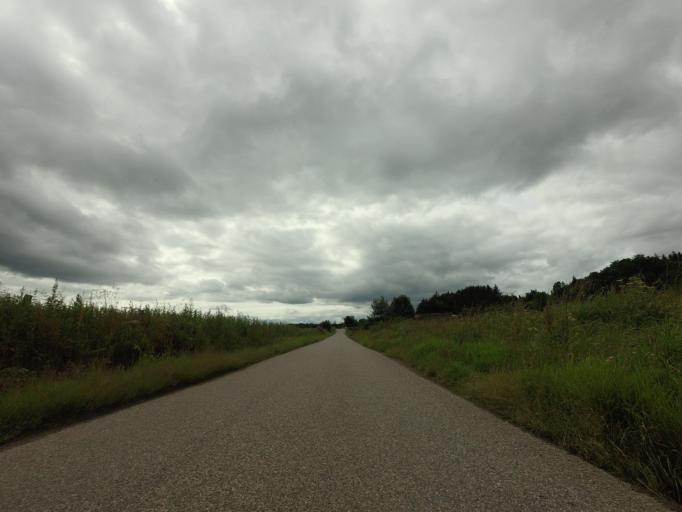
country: GB
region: Scotland
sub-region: Moray
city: Forres
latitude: 57.6012
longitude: -3.6948
